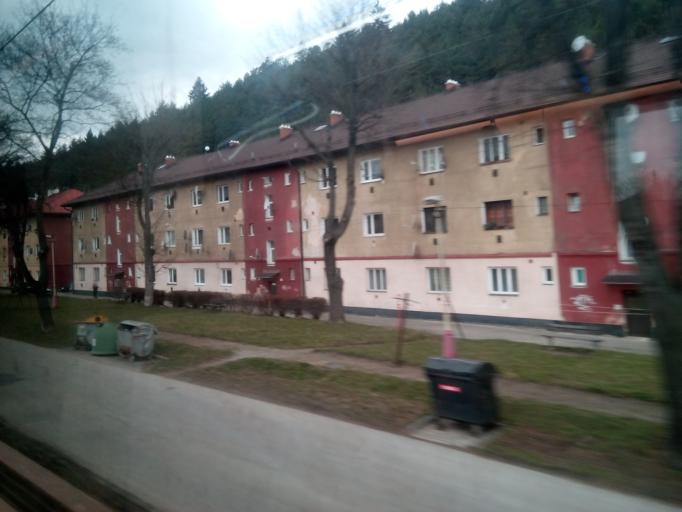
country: SK
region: Zilinsky
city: Ruzomberok
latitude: 49.0871
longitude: 19.2950
